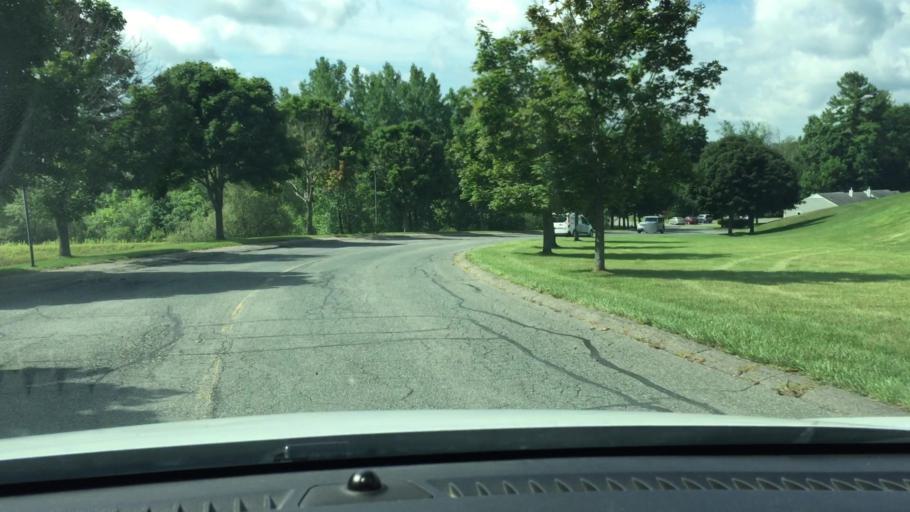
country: US
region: Massachusetts
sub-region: Berkshire County
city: Pittsfield
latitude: 42.4541
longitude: -73.2799
